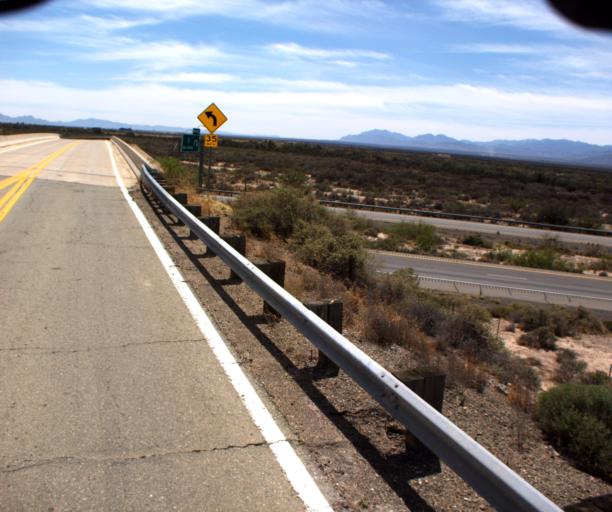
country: US
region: New Mexico
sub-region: Hidalgo County
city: Lordsburg
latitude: 32.2579
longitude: -109.1955
